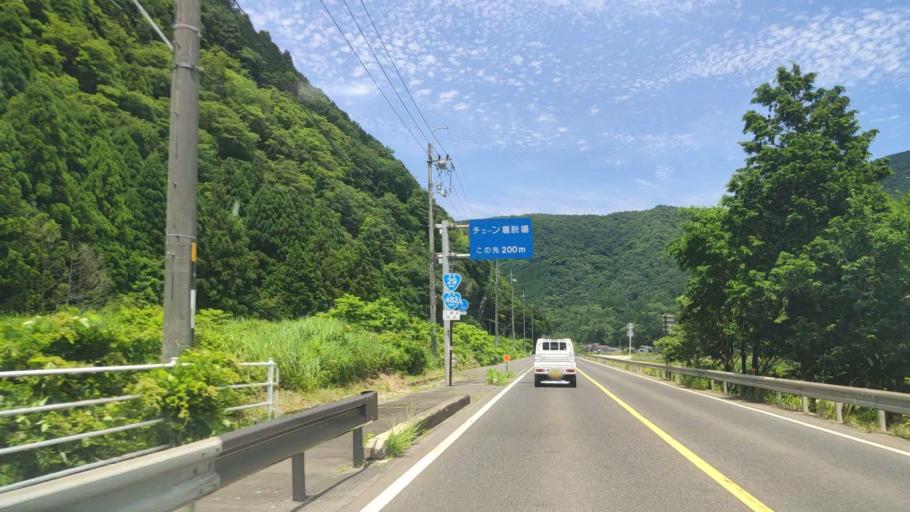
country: JP
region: Tottori
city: Tottori
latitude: 35.3617
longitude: 134.3782
